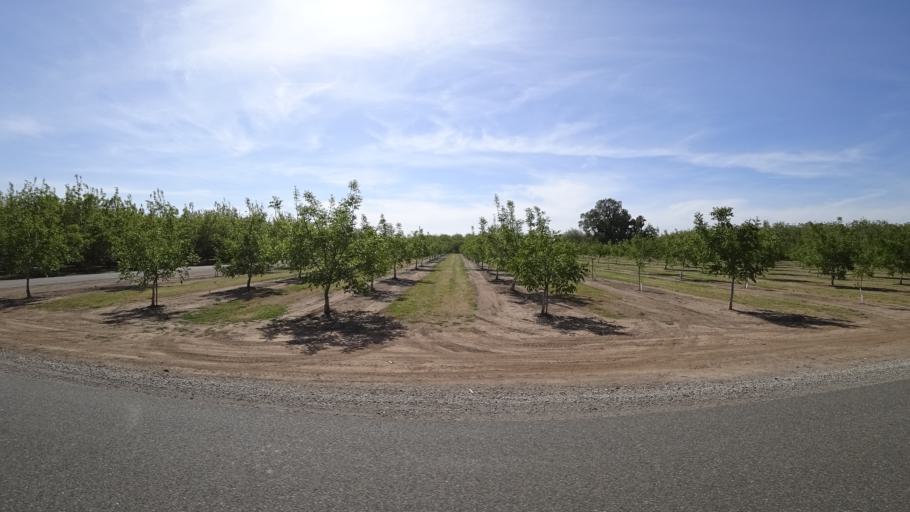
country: US
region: California
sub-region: Tehama County
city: Los Molinos
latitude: 40.0711
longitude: -122.1007
